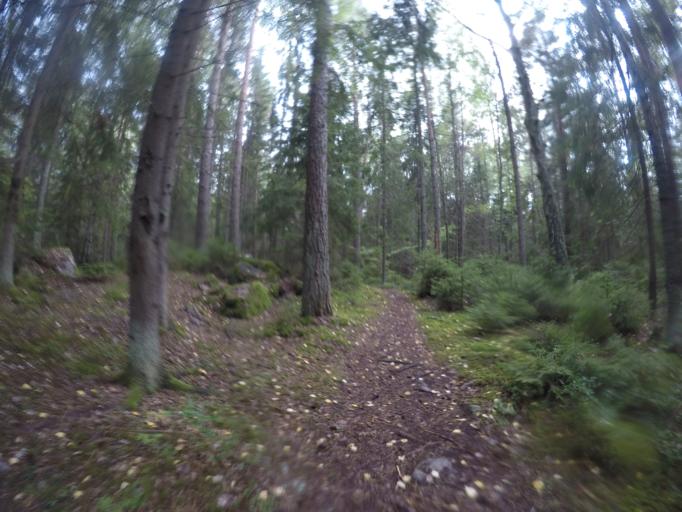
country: SE
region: Vaestmanland
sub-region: Vasteras
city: Vasteras
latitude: 59.6482
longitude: 16.5184
